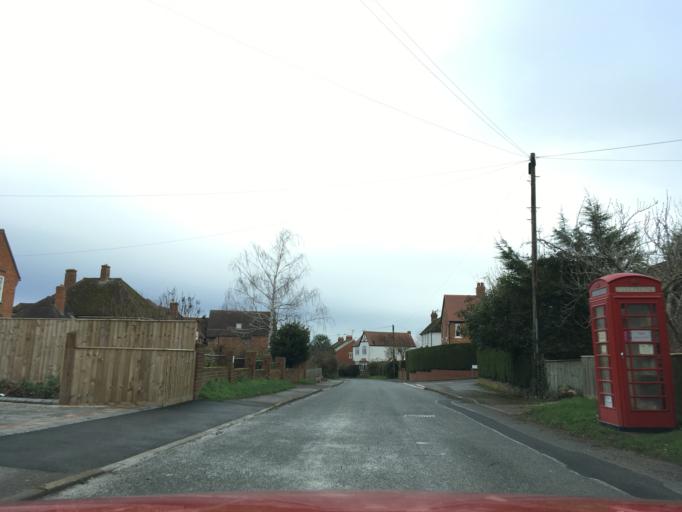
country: GB
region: England
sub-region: Worcestershire
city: Evesham
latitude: 52.0441
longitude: -1.9681
